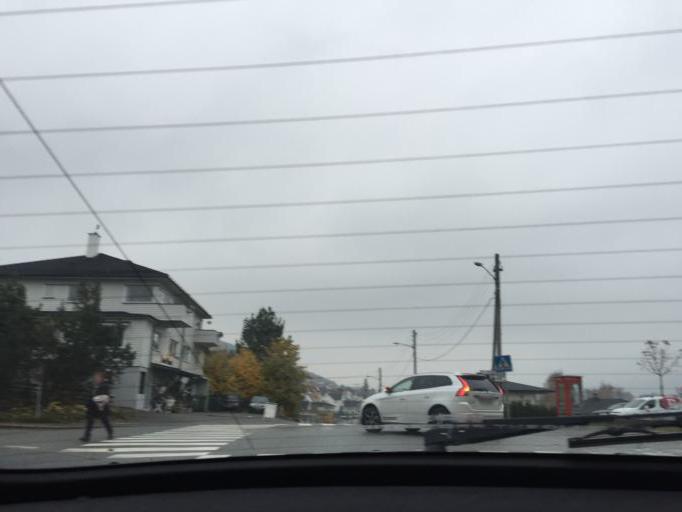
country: NO
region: Buskerud
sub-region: Drammen
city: Drammen
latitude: 59.7297
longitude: 10.2054
